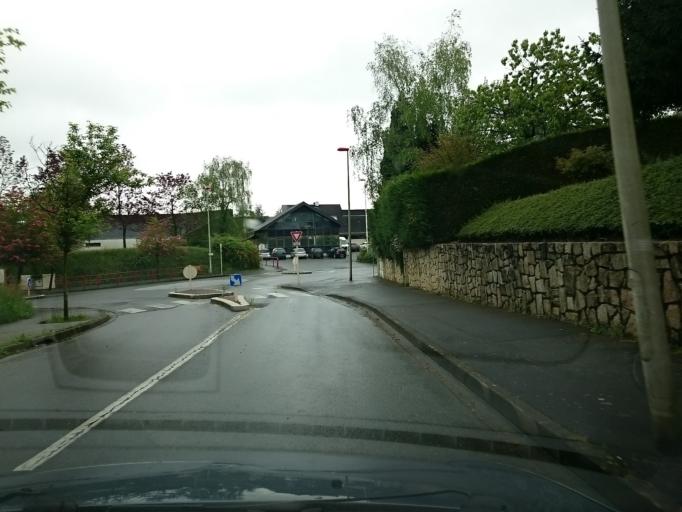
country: FR
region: Brittany
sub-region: Departement d'Ille-et-Vilaine
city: Saint-Gregoire
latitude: 48.1501
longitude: -1.6847
